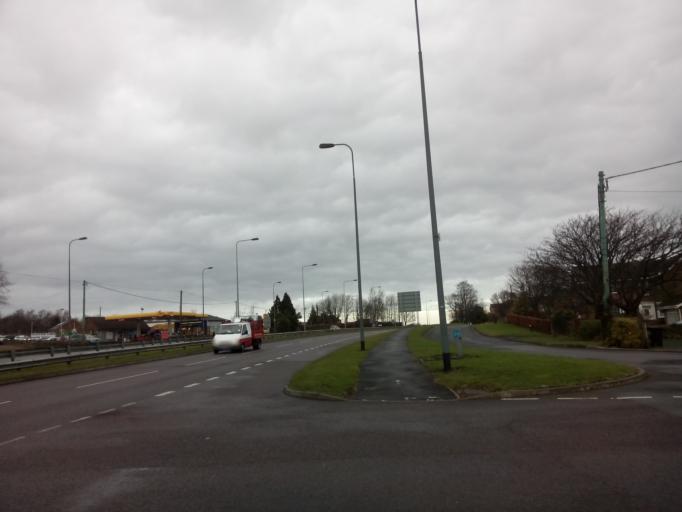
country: GB
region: England
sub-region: County Durham
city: Sacriston
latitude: 54.8256
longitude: -1.5937
